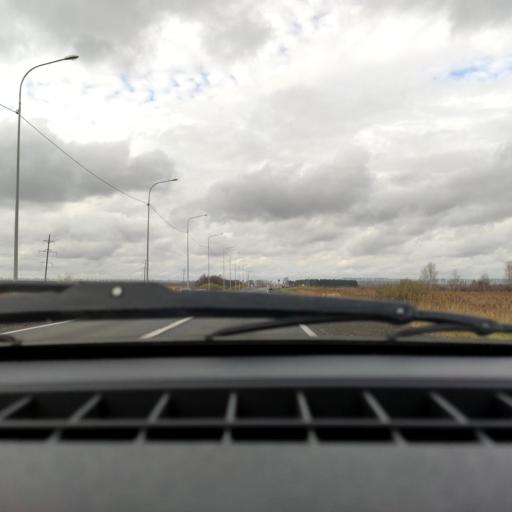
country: RU
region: Bashkortostan
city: Asanovo
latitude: 54.9120
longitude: 55.5955
